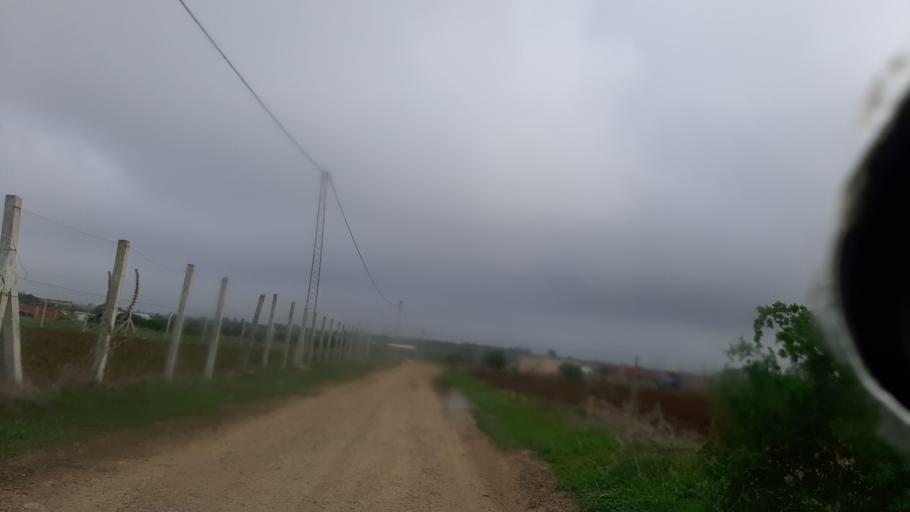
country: TN
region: Nabul
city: Qulaybiyah
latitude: 36.8325
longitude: 11.0364
